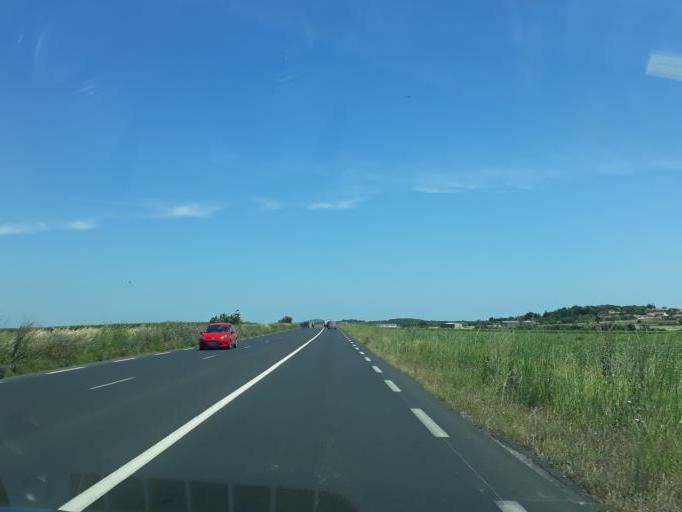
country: FR
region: Languedoc-Roussillon
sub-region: Departement de l'Herault
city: Portiragnes
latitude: 43.3134
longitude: 3.3265
